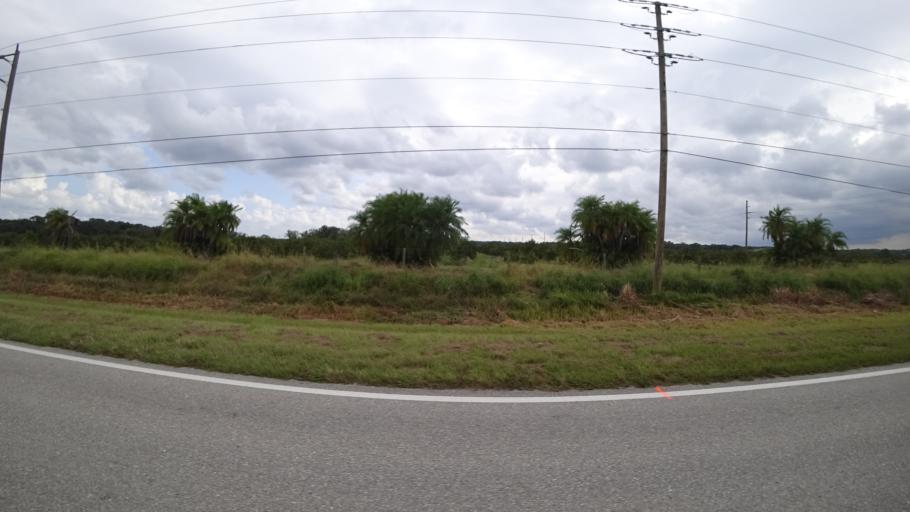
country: US
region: Florida
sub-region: Manatee County
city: Ellenton
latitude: 27.6012
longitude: -82.4776
